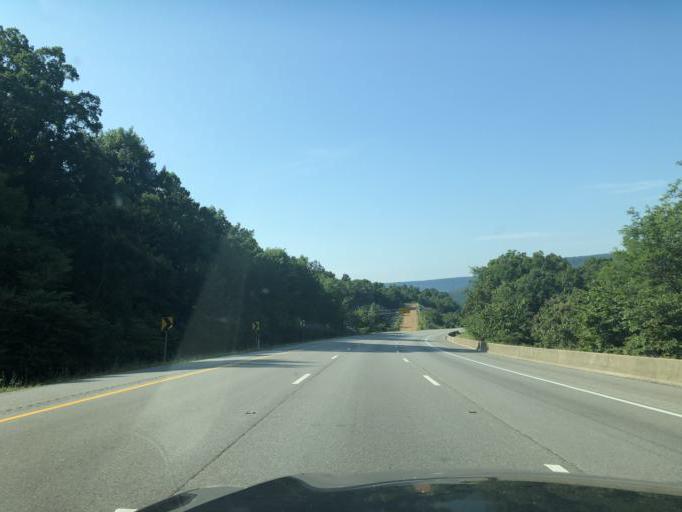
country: US
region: Tennessee
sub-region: Marion County
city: Monteagle
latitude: 35.1999
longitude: -85.8134
